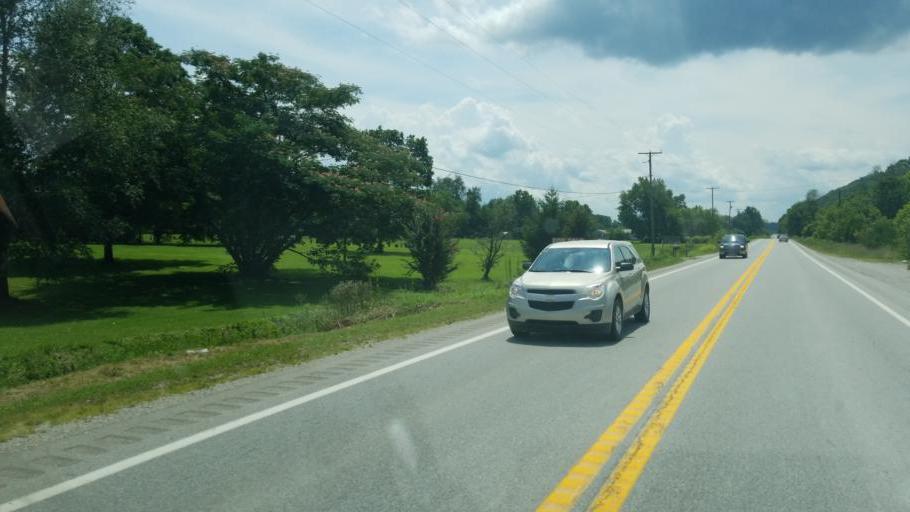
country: US
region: West Virginia
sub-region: Putnam County
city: Buffalo
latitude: 38.6228
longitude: -81.9858
